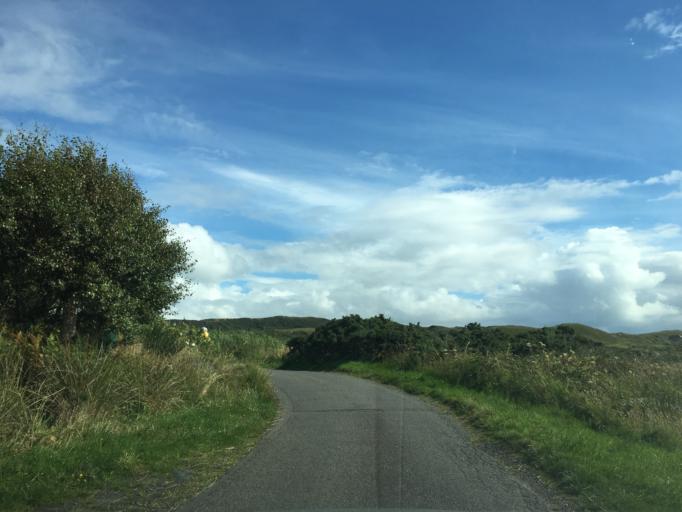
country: GB
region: Scotland
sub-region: Argyll and Bute
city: Isle Of Mull
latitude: 56.2493
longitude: -5.6519
